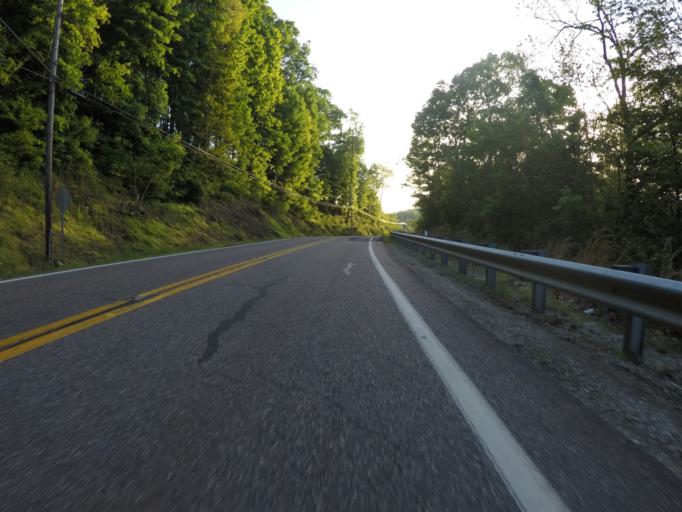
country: US
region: West Virginia
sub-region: Cabell County
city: Huntington
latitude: 38.5215
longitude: -82.4691
